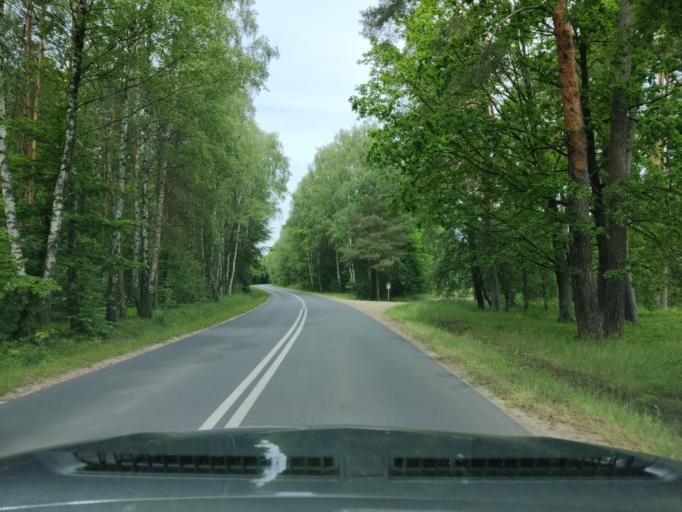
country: PL
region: Masovian Voivodeship
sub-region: Powiat wyszkowski
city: Rzasnik
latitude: 52.6767
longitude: 21.4232
